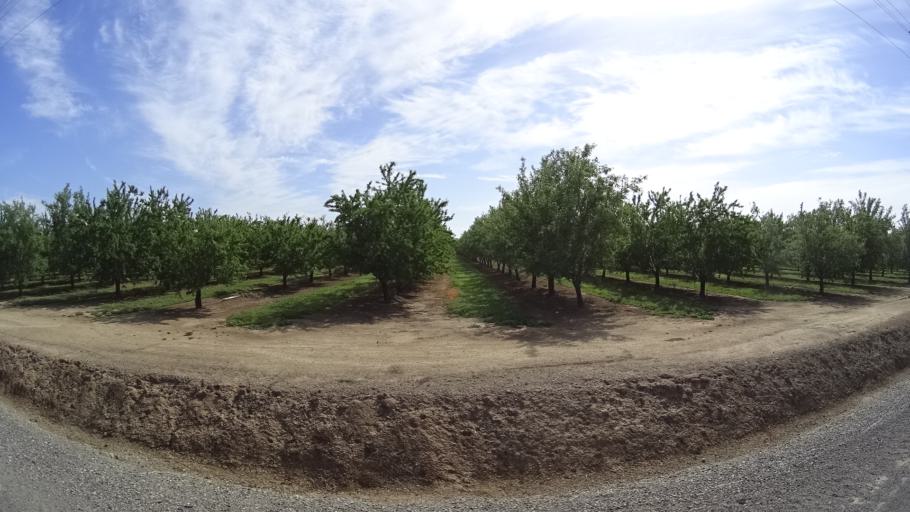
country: US
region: California
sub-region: Glenn County
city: Hamilton City
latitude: 39.6375
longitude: -122.0073
